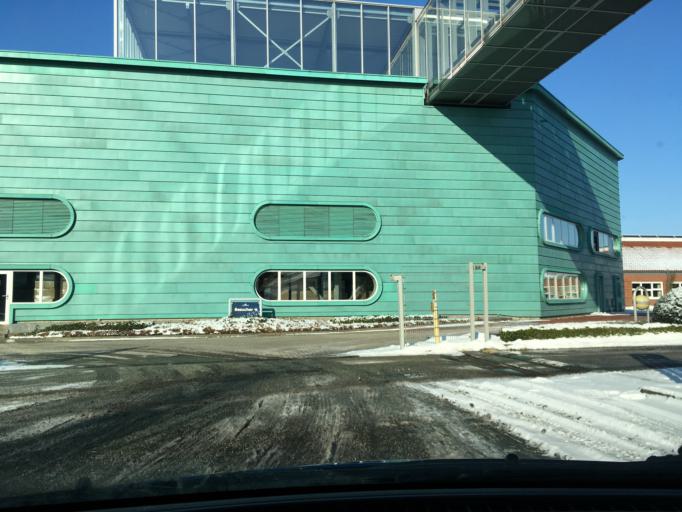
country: DE
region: Schleswig-Holstein
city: Escheburg
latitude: 53.4367
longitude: 10.3294
